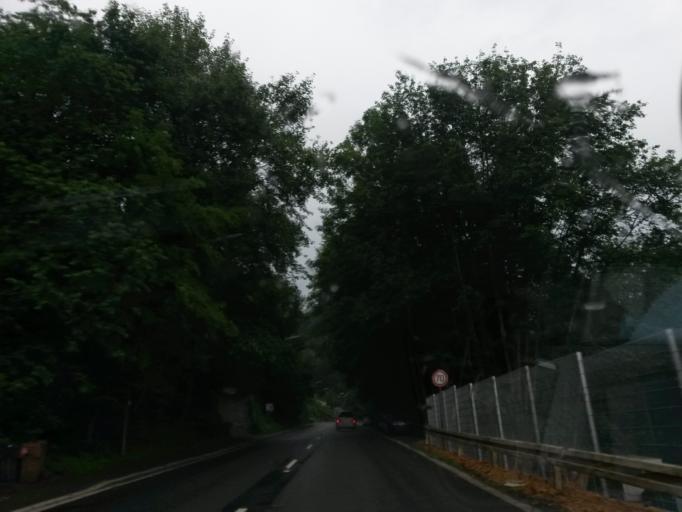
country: DE
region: North Rhine-Westphalia
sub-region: Regierungsbezirk Koln
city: Gummersbach
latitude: 51.0326
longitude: 7.5569
